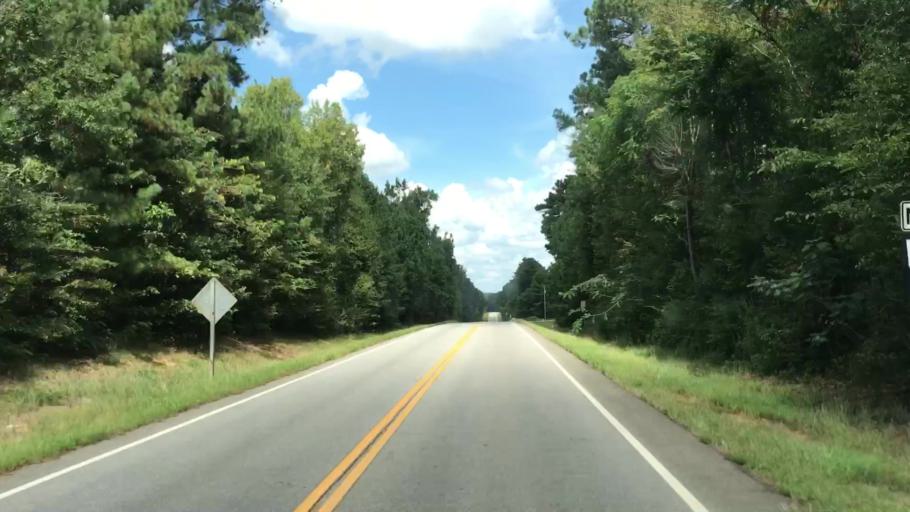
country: US
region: Georgia
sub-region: Greene County
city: Greensboro
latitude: 33.6194
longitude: -83.2115
